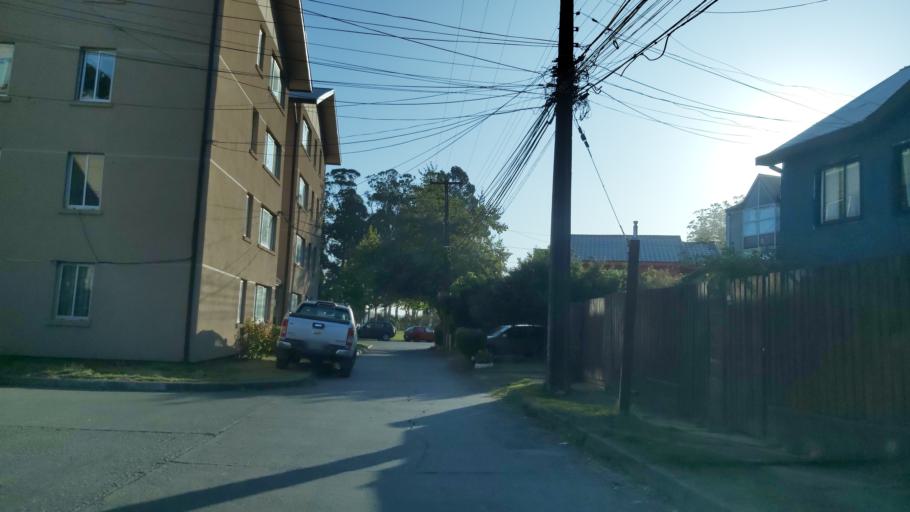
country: CL
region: Biobio
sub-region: Provincia de Concepcion
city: Concepcion
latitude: -36.8451
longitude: -73.1054
